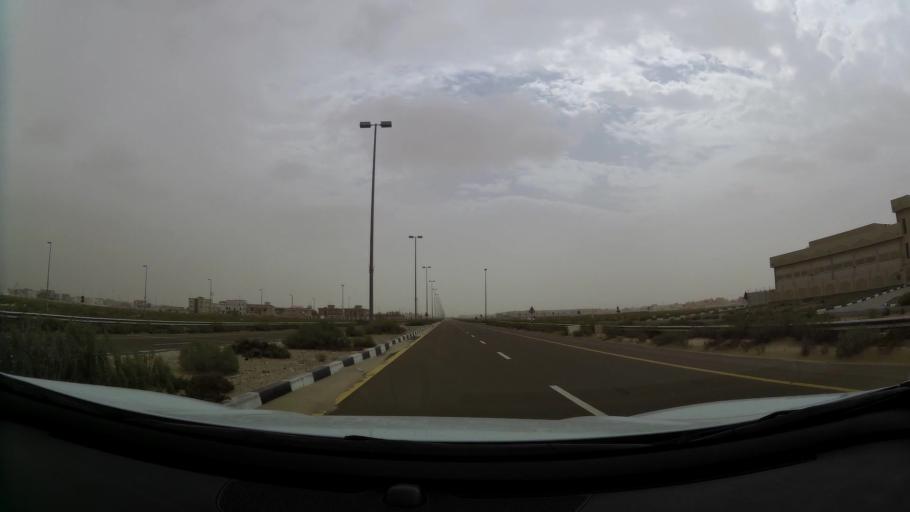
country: AE
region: Abu Dhabi
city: Abu Dhabi
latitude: 24.3700
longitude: 54.6869
